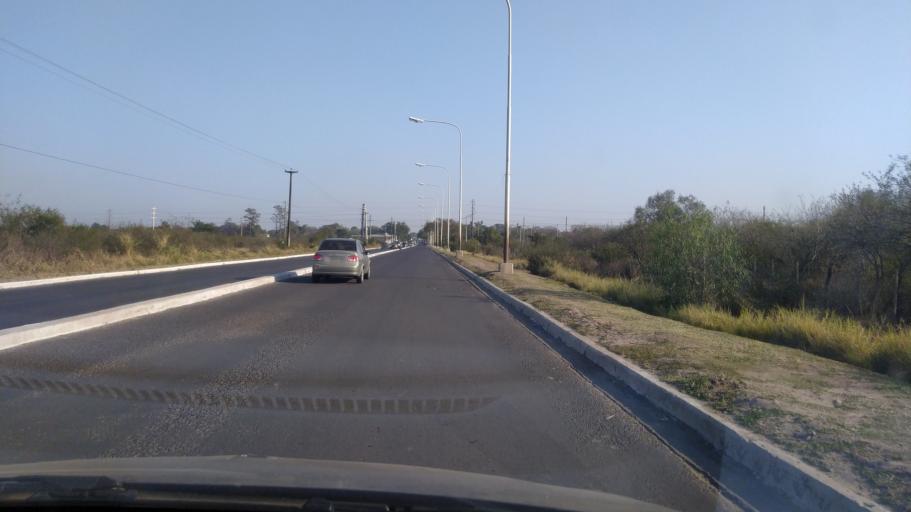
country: AR
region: Corrientes
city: Corrientes
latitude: -27.5181
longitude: -58.8024
